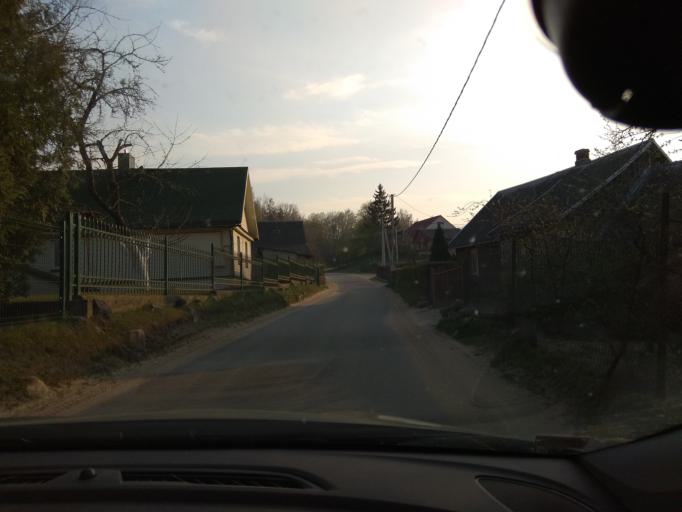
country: LT
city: Baltoji Voke
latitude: 54.5945
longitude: 25.1751
